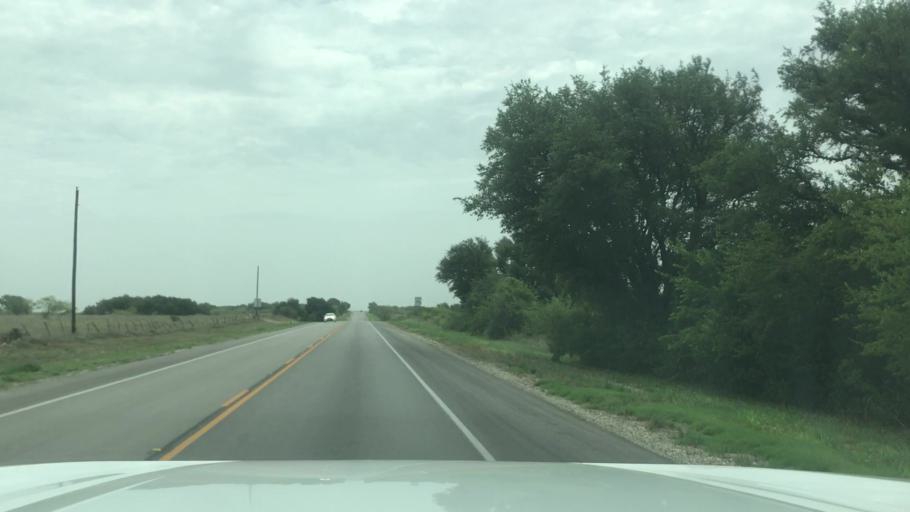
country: US
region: Texas
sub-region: Erath County
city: Dublin
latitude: 32.0836
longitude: -98.2500
